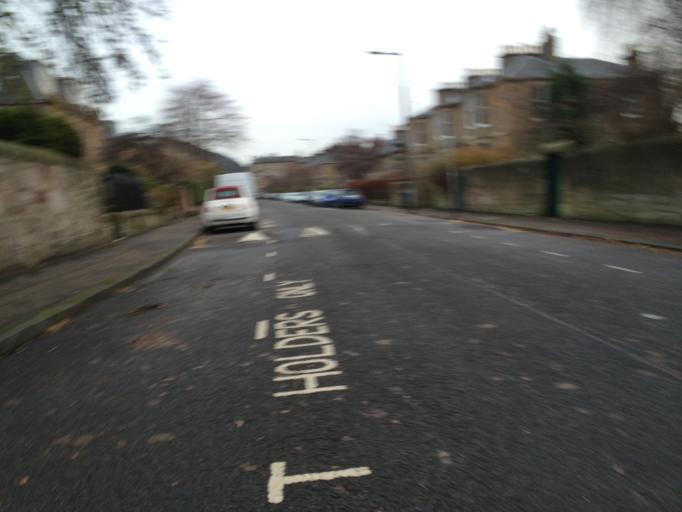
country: GB
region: Scotland
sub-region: Edinburgh
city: Edinburgh
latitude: 55.9324
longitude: -3.1829
